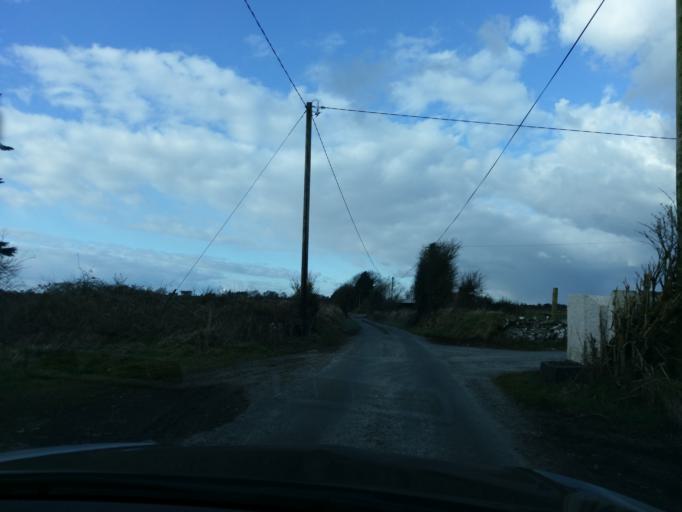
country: IE
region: Connaught
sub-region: County Galway
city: Athenry
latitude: 53.4572
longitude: -8.6434
